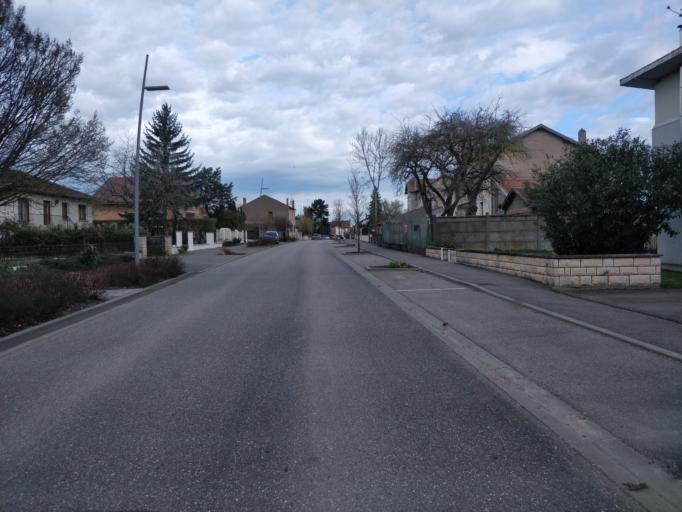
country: FR
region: Lorraine
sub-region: Departement de Meurthe-et-Moselle
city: Jarny
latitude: 49.0954
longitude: 5.8900
